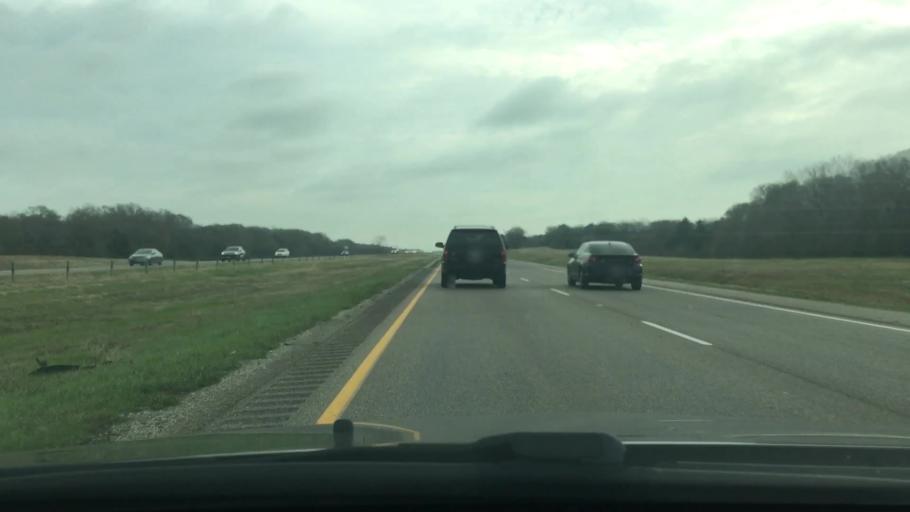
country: US
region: Texas
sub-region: Freestone County
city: Fairfield
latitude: 31.6260
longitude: -96.1577
